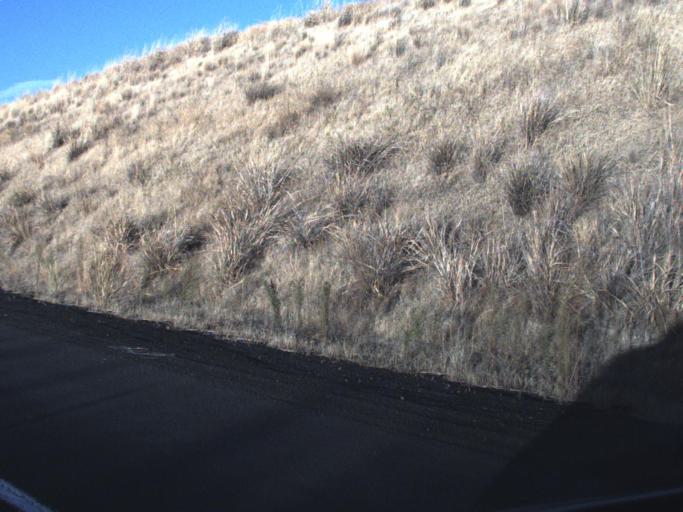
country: US
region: Washington
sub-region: Adams County
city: Ritzville
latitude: 47.1087
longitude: -118.3934
